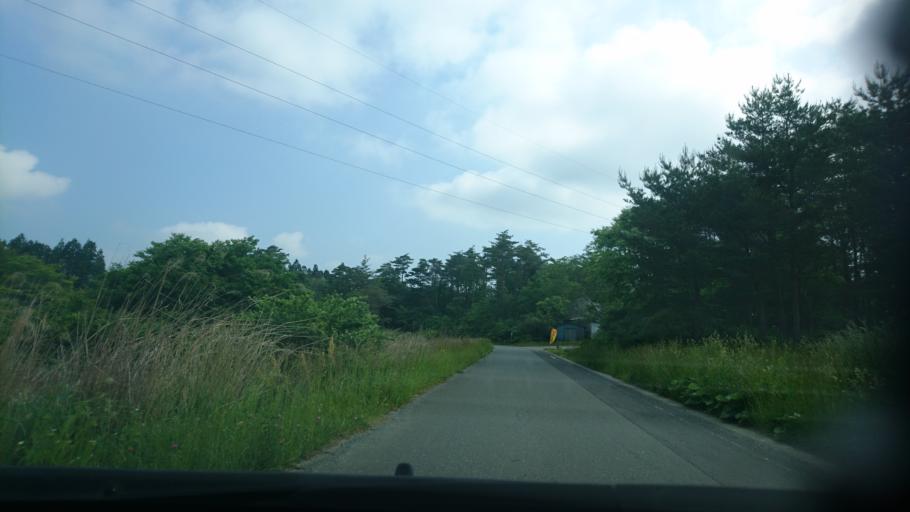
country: JP
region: Iwate
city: Ichinoseki
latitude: 38.8999
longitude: 141.2406
